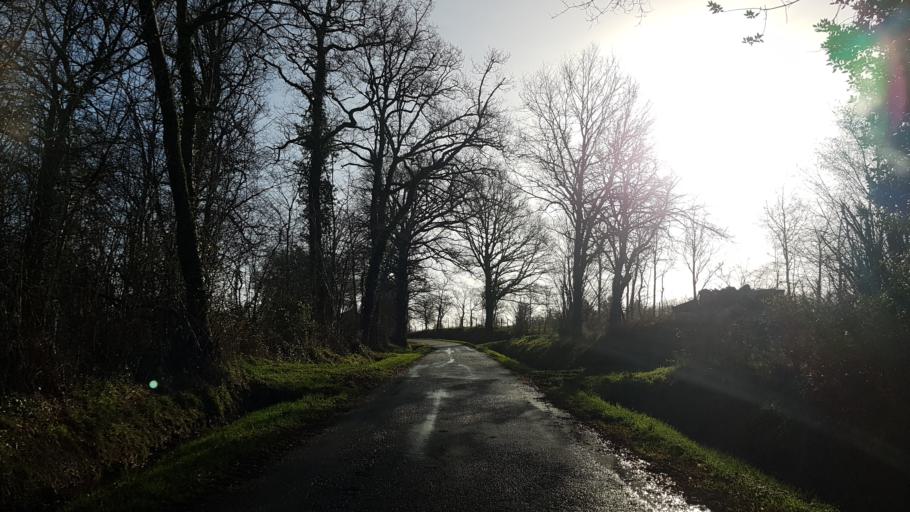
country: FR
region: Poitou-Charentes
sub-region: Departement de la Charente
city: Etagnac
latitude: 45.9224
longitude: 0.8184
